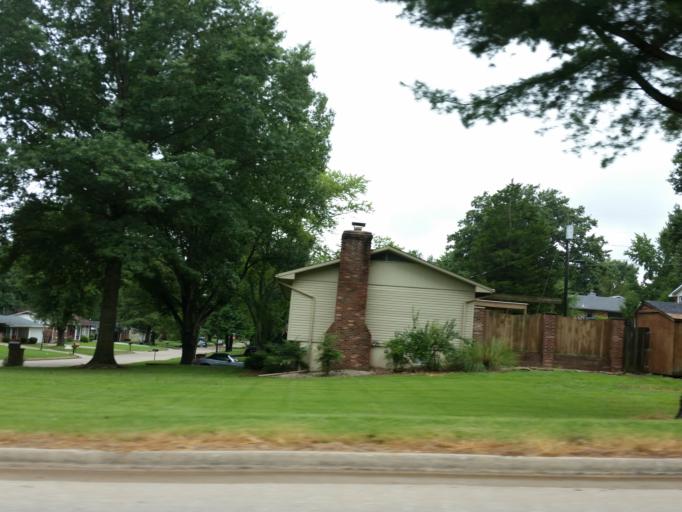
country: US
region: Missouri
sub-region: Cape Girardeau County
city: Cape Girardeau
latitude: 37.3338
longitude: -89.5474
